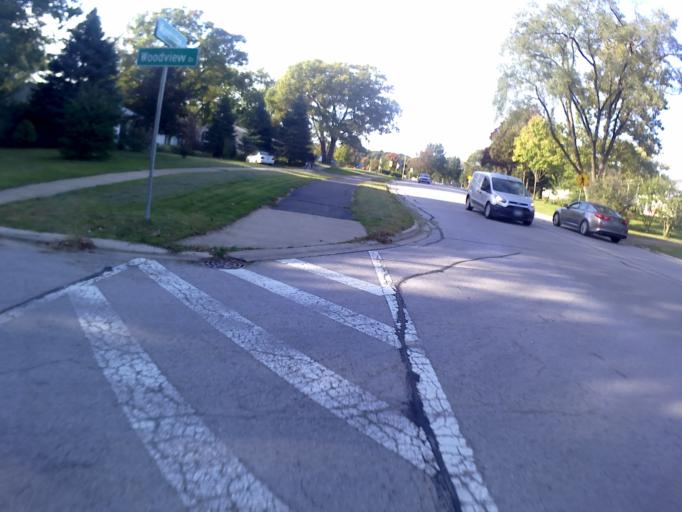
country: US
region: Illinois
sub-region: DuPage County
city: Woodridge
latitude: 41.7479
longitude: -88.0516
